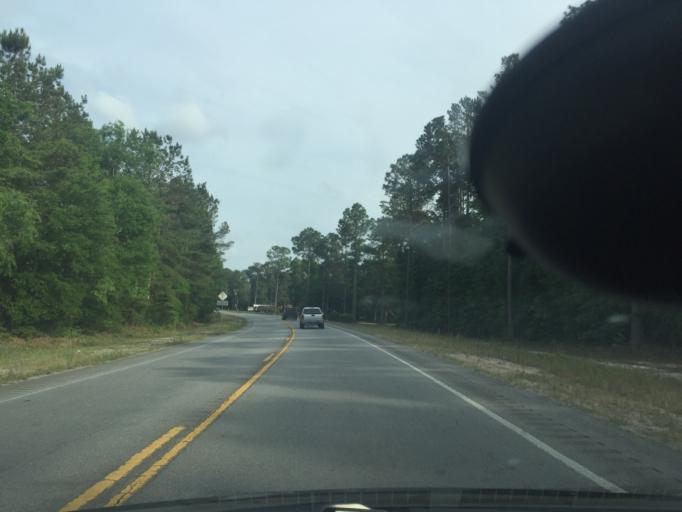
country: US
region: Georgia
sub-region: Chatham County
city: Bloomingdale
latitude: 32.0775
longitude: -81.3685
